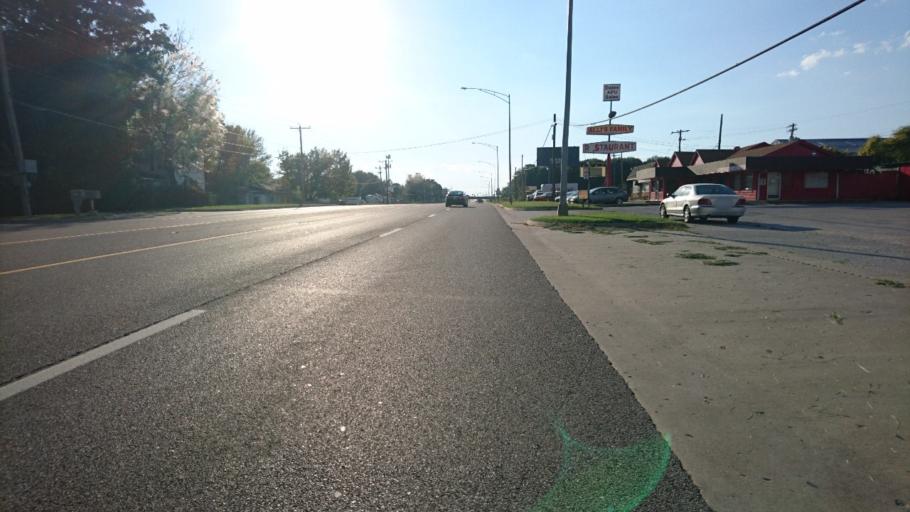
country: US
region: Missouri
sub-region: Greene County
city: Springfield
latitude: 37.2125
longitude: -93.3723
